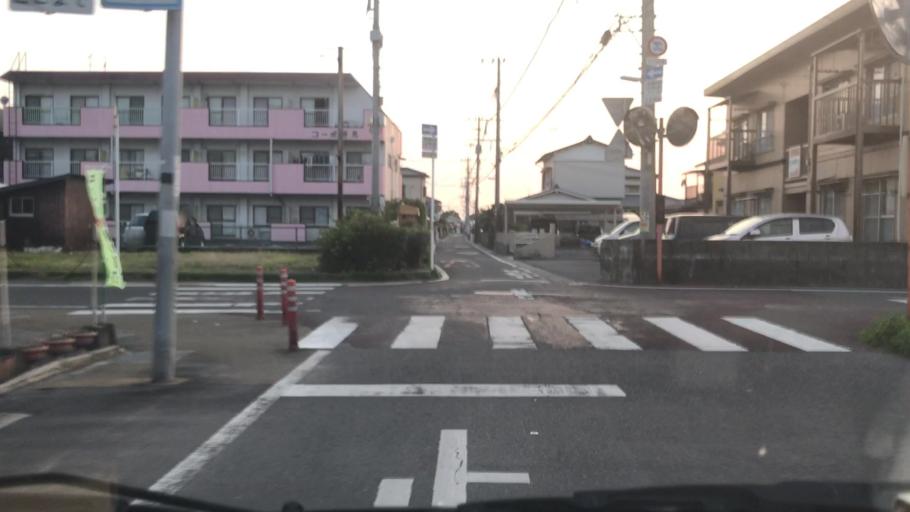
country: JP
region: Saga Prefecture
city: Saga-shi
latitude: 33.2513
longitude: 130.2804
